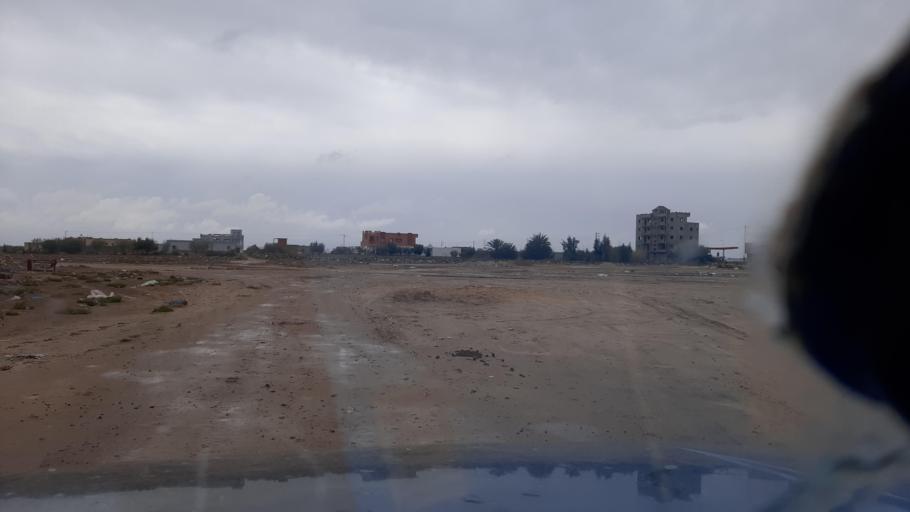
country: TN
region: Al Mahdiyah
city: Shurban
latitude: 35.4356
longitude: 10.3963
